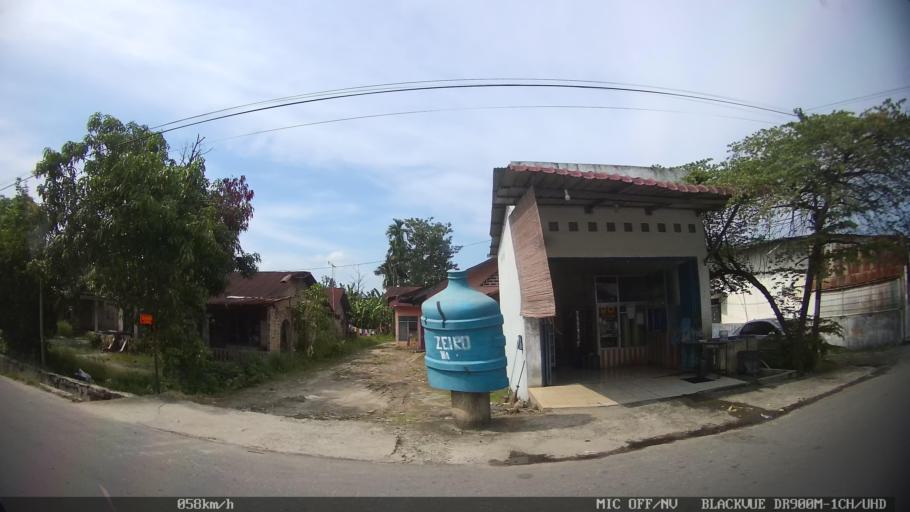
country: ID
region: North Sumatra
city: Percut
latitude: 3.6120
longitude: 98.8128
